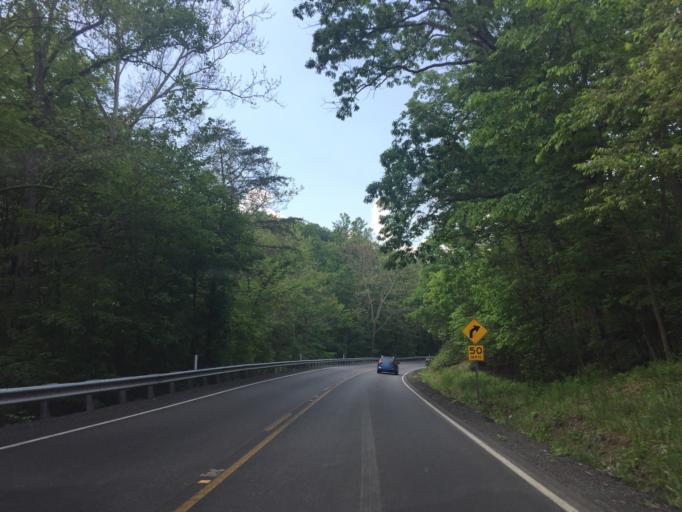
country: US
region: Virginia
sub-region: Shenandoah County
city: Woodstock
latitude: 39.0864
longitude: -78.5474
